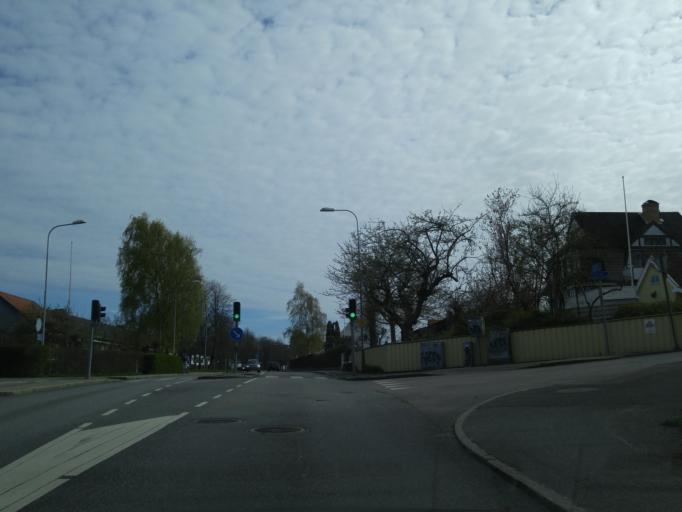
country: SE
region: Vaestra Goetaland
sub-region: Goteborg
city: Majorna
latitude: 57.6673
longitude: 11.8723
